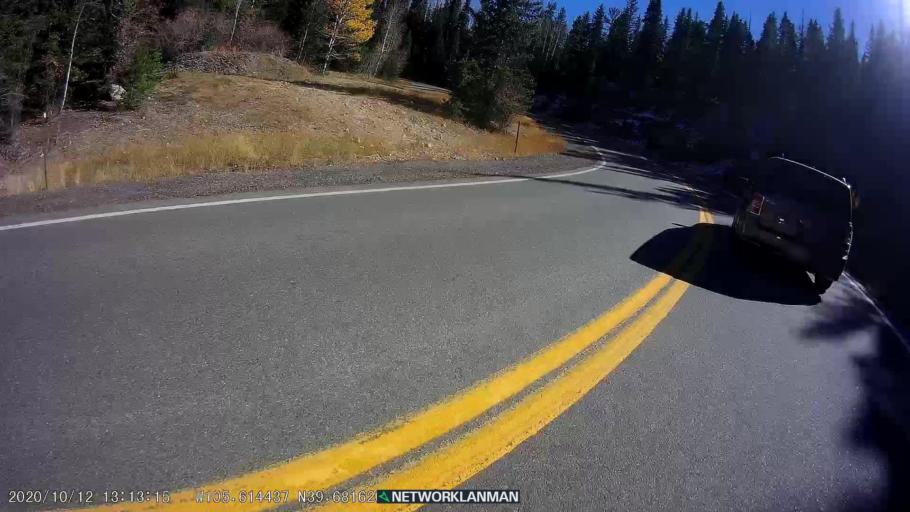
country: US
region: Colorado
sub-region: Clear Creek County
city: Georgetown
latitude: 39.6815
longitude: -105.6149
